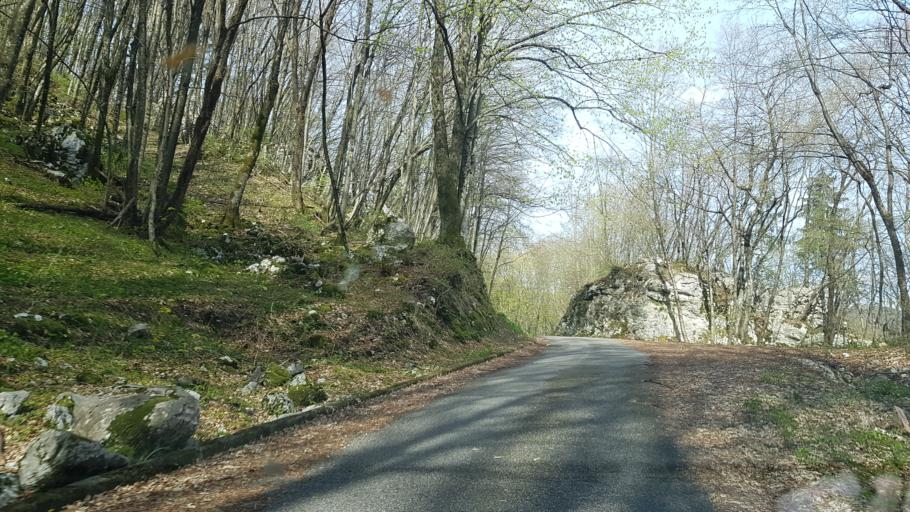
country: IT
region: Friuli Venezia Giulia
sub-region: Provincia di Udine
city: Trasaghis
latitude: 46.2859
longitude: 13.0311
